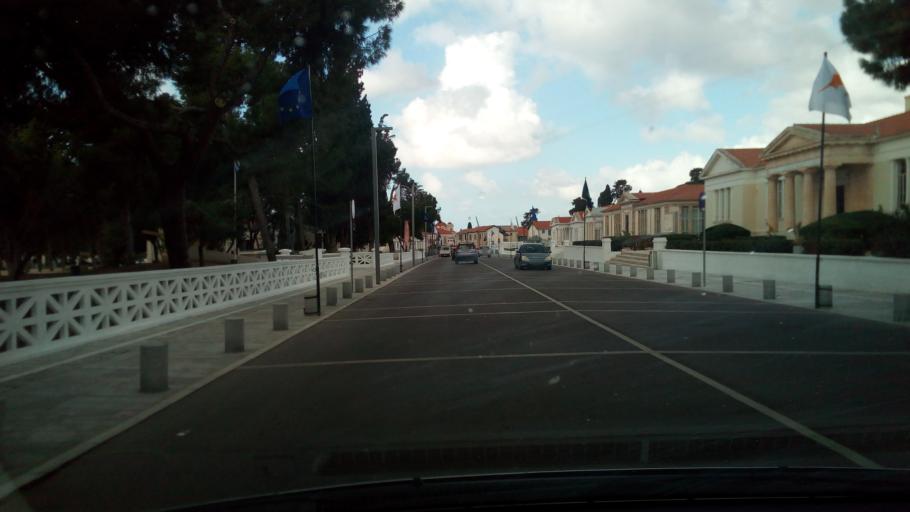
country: CY
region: Pafos
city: Paphos
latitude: 34.7738
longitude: 32.4241
